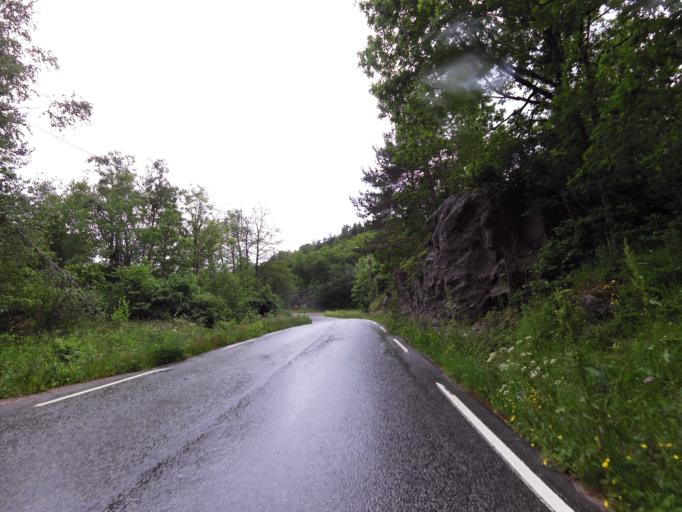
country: NO
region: Vest-Agder
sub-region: Mandal
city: Mandal
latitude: 58.0126
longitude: 7.5117
